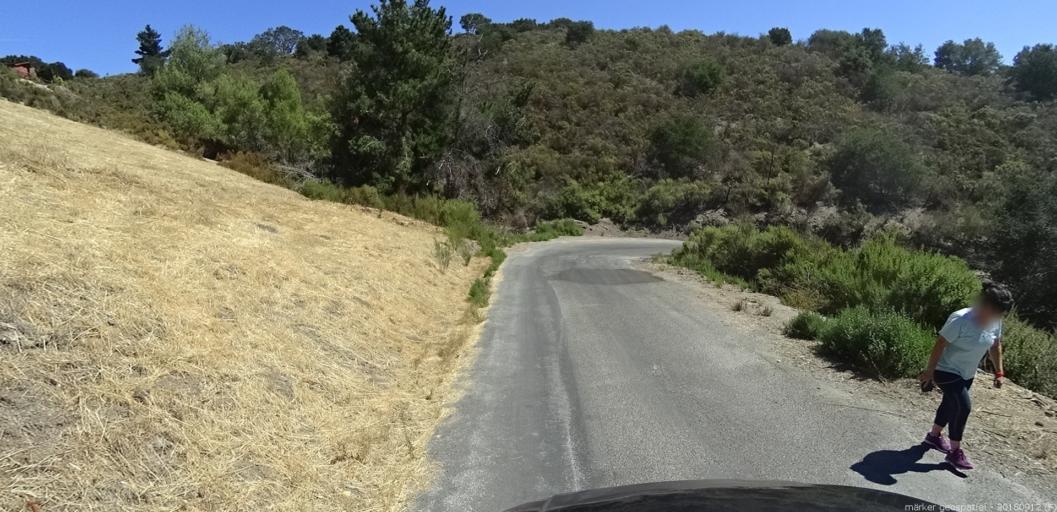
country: US
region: California
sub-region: Monterey County
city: Carmel Valley Village
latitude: 36.4871
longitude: -121.7219
